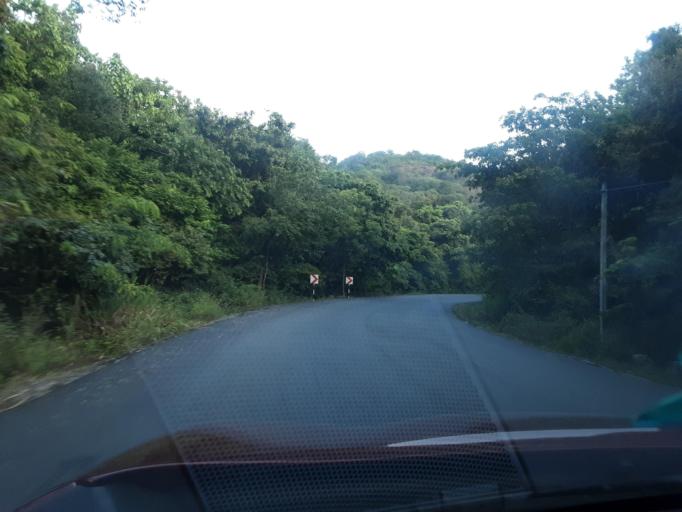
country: LK
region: Central
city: Dambulla
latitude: 7.8142
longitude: 80.7659
